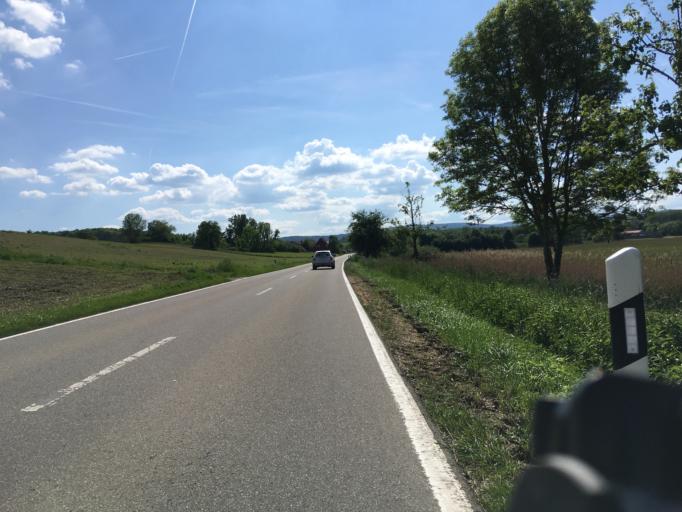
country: CH
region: Schaffhausen
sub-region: Bezirk Reiat
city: Thayngen
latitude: 47.7970
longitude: 8.7230
